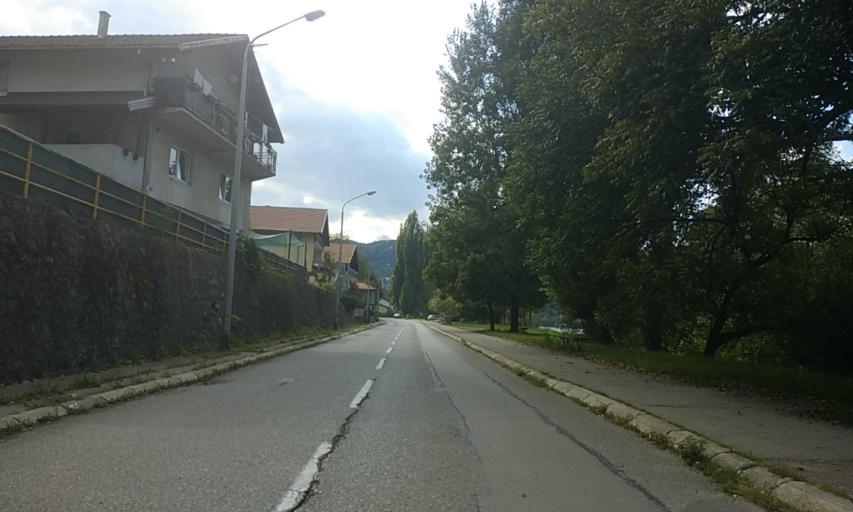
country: BA
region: Republika Srpska
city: Hiseti
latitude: 44.7512
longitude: 17.1705
